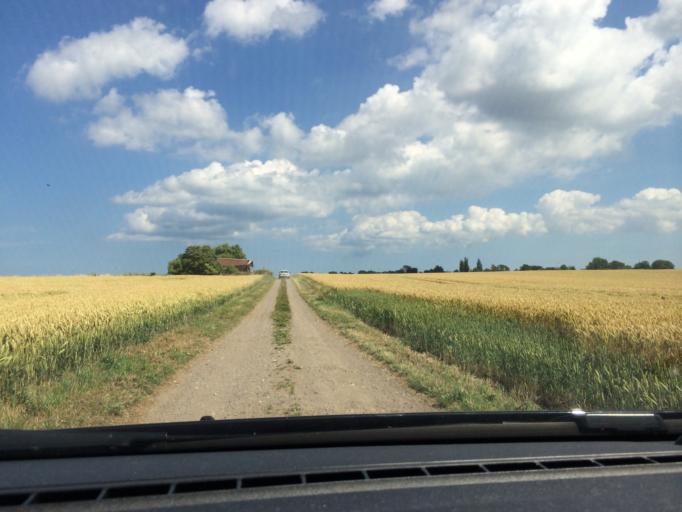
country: DK
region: Zealand
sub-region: Vordingborg Kommune
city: Stege
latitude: 55.0435
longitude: 12.1850
